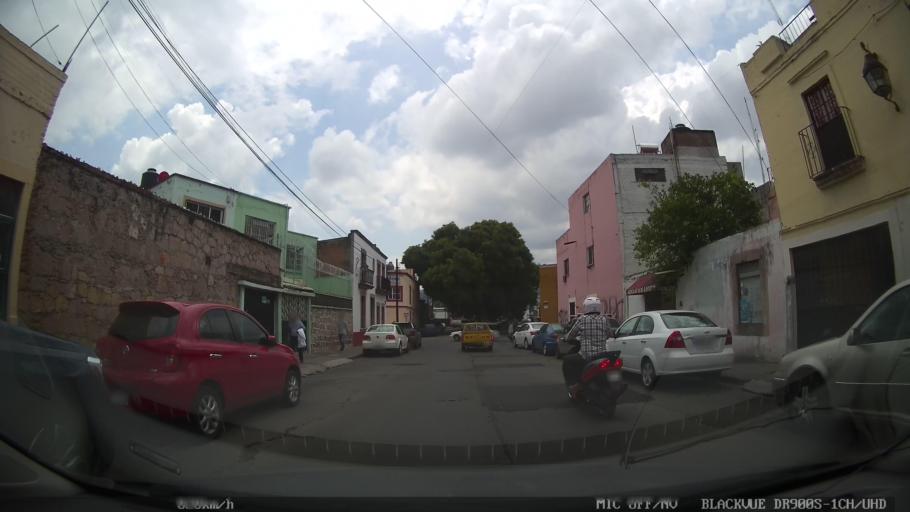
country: MX
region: Michoacan
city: Morelia
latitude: 19.6995
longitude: -101.1859
